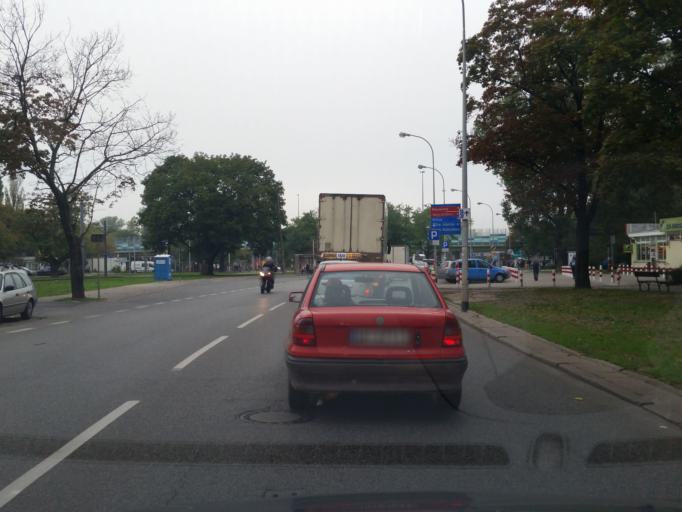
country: PL
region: Masovian Voivodeship
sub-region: Warszawa
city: Praga Polnoc
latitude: 52.2619
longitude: 21.0226
